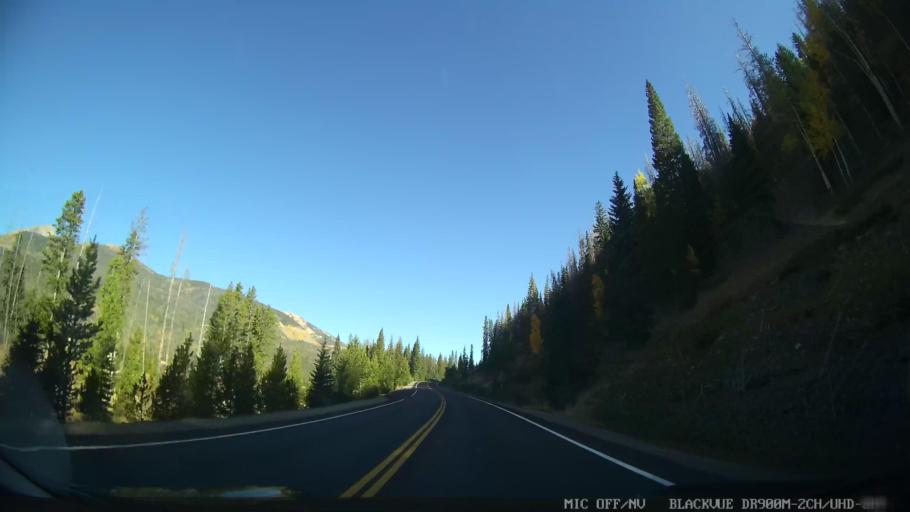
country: US
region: Colorado
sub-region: Grand County
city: Granby
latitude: 40.3587
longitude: -105.8556
